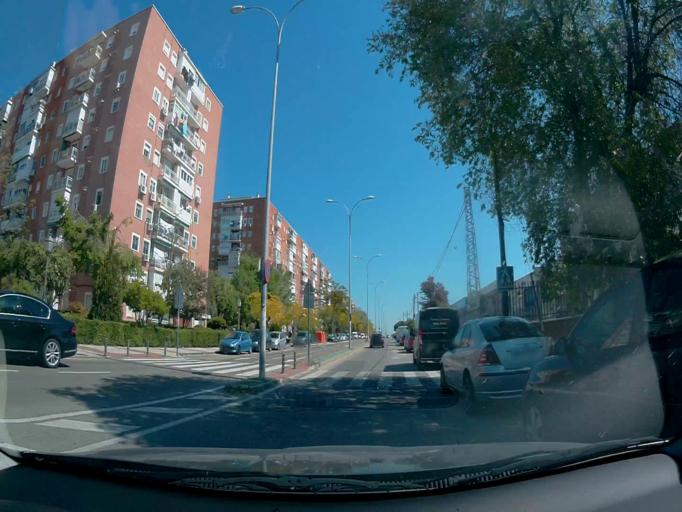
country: ES
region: Madrid
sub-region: Provincia de Madrid
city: Alcorcon
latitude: 40.3495
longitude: -3.8027
